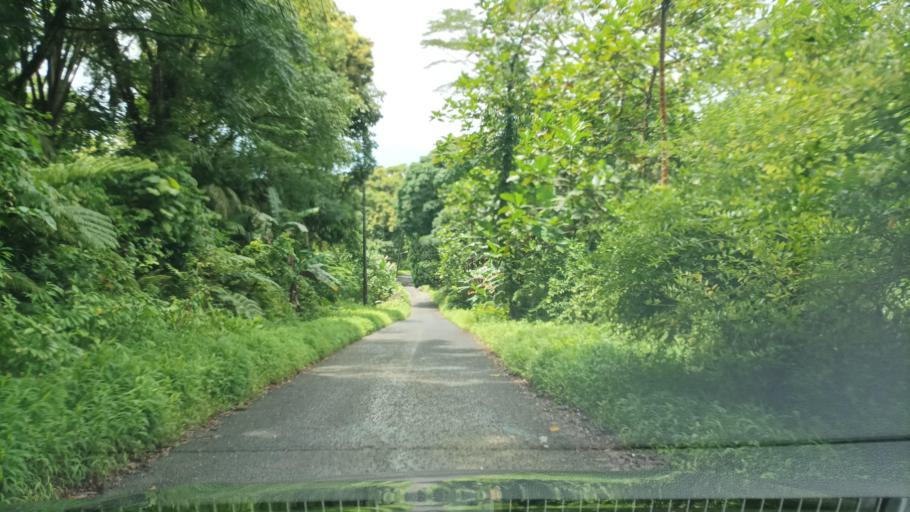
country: FM
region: Pohnpei
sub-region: Kolonia Municipality
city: Kolonia
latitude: 6.9614
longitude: 158.2250
